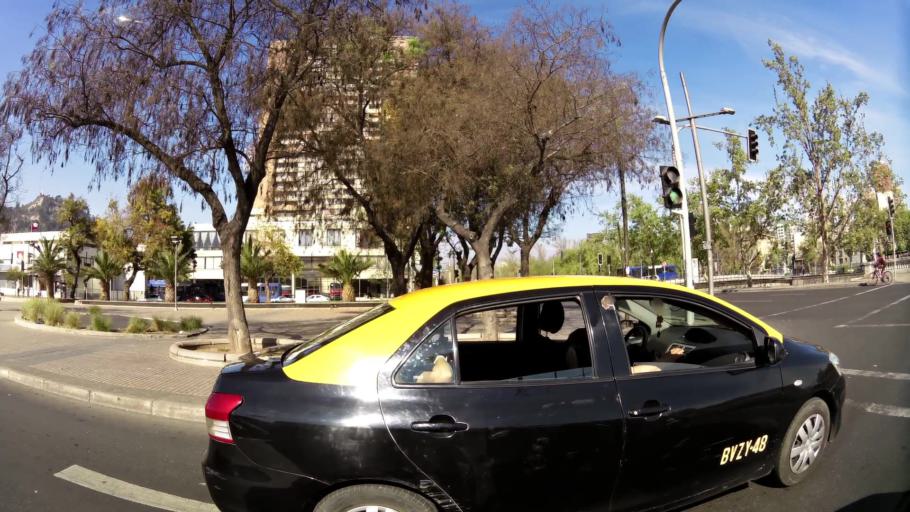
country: CL
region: Santiago Metropolitan
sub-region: Provincia de Santiago
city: Santiago
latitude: -33.4325
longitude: -70.6485
